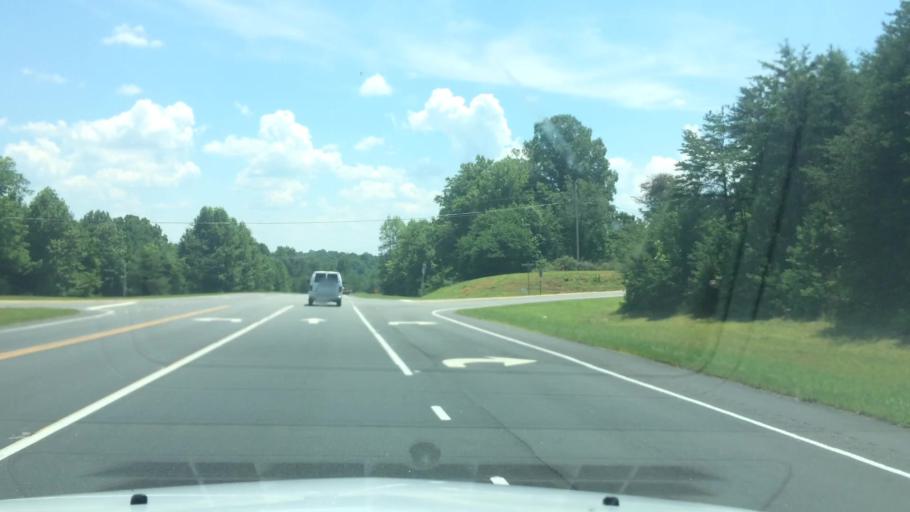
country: US
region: North Carolina
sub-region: Alexander County
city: Stony Point
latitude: 35.8365
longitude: -81.0205
